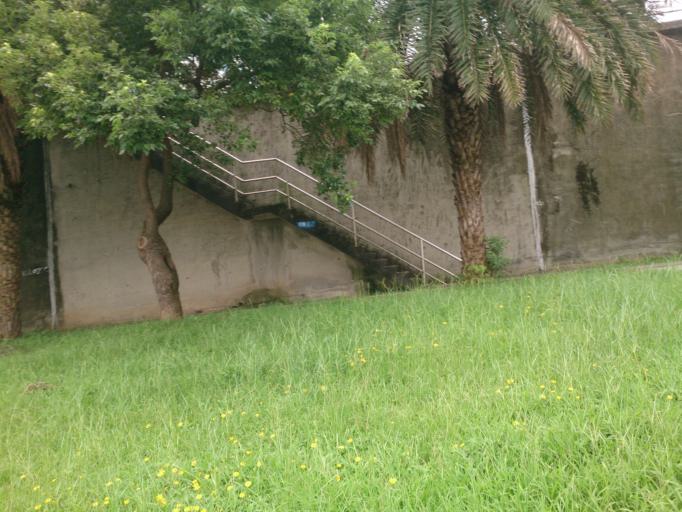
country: TW
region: Taipei
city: Taipei
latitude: 25.0562
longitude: 121.5899
